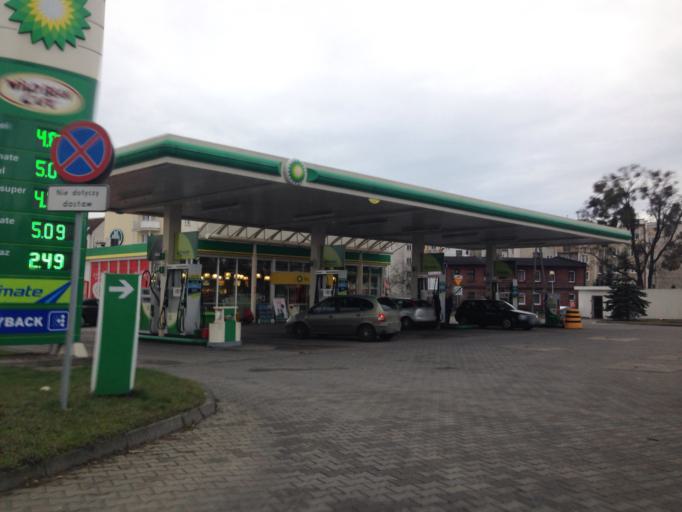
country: PL
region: Kujawsko-Pomorskie
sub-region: Torun
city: Torun
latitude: 53.0325
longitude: 18.6107
